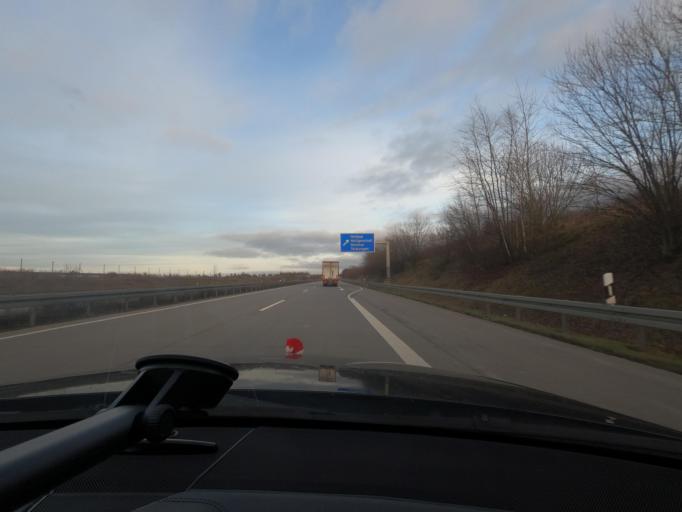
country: DE
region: Thuringia
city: Heilbad Heiligenstadt
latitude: 51.3947
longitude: 10.1246
